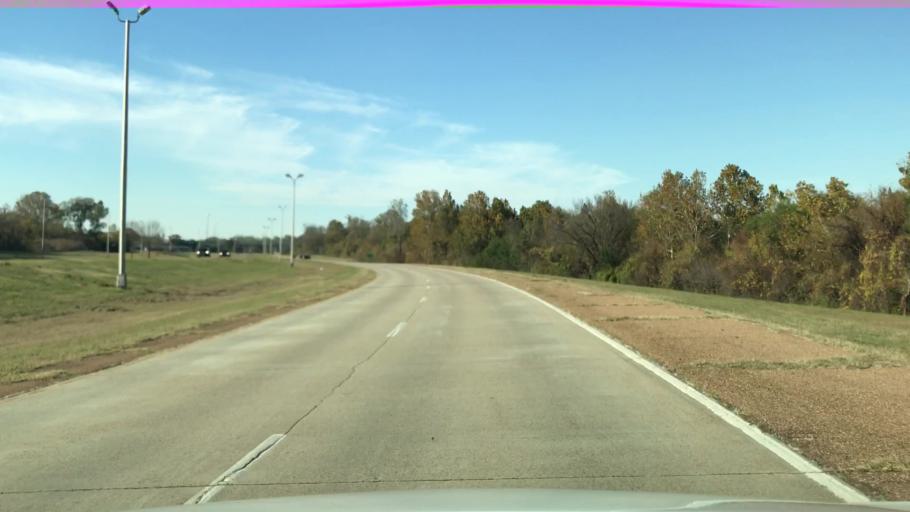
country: US
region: Louisiana
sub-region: Bossier Parish
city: Bossier City
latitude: 32.4845
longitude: -93.6940
